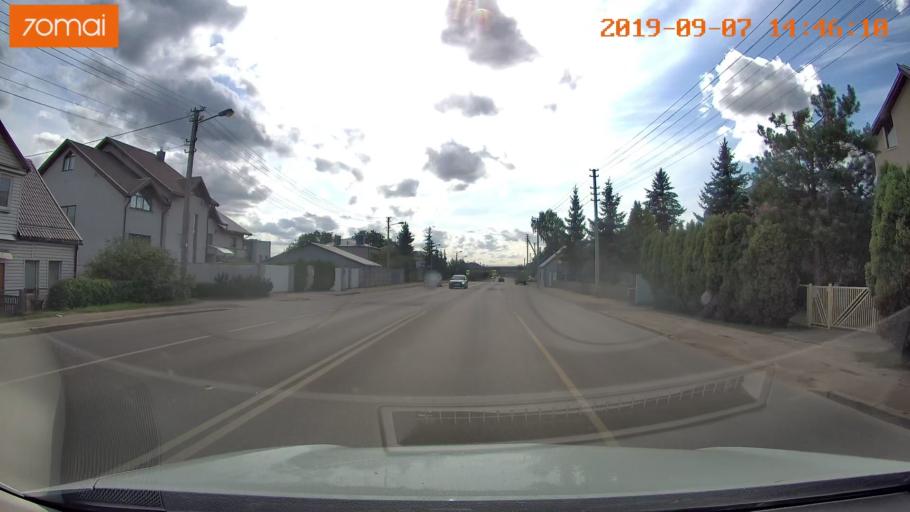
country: LT
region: Kauno apskritis
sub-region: Kaunas
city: Silainiai
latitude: 54.9276
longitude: 23.9059
